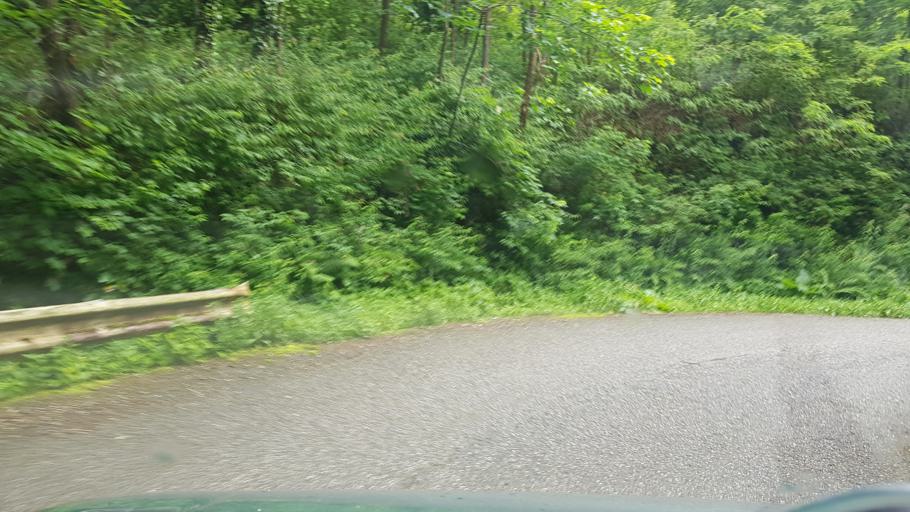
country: IT
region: Friuli Venezia Giulia
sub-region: Provincia di Gorizia
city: San Floriano del Collio
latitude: 45.9500
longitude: 13.5907
